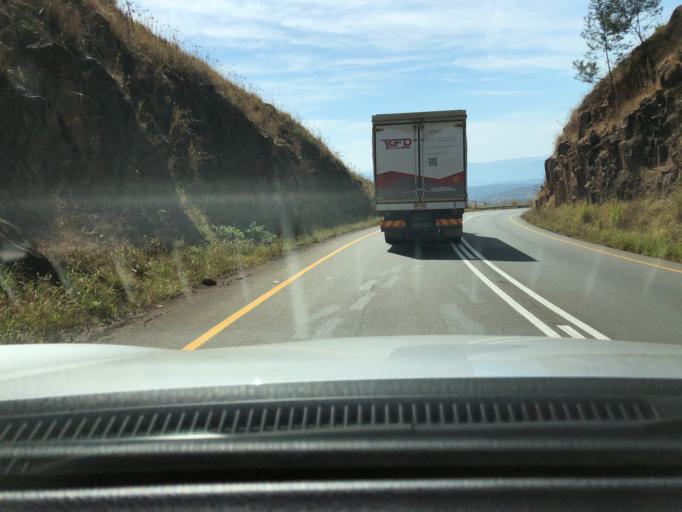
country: ZA
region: KwaZulu-Natal
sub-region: Sisonke District Municipality
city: Ixopo
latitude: -30.0552
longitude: 30.1896
